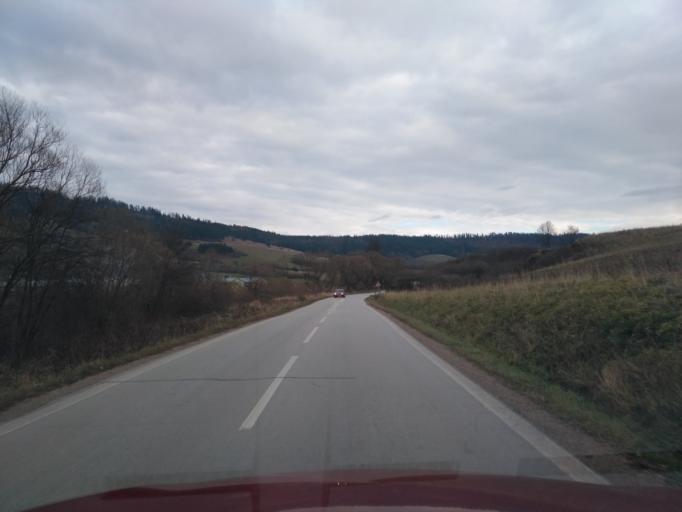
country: SK
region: Kosicky
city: Spisska Nova Ves
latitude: 48.8378
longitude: 20.6408
